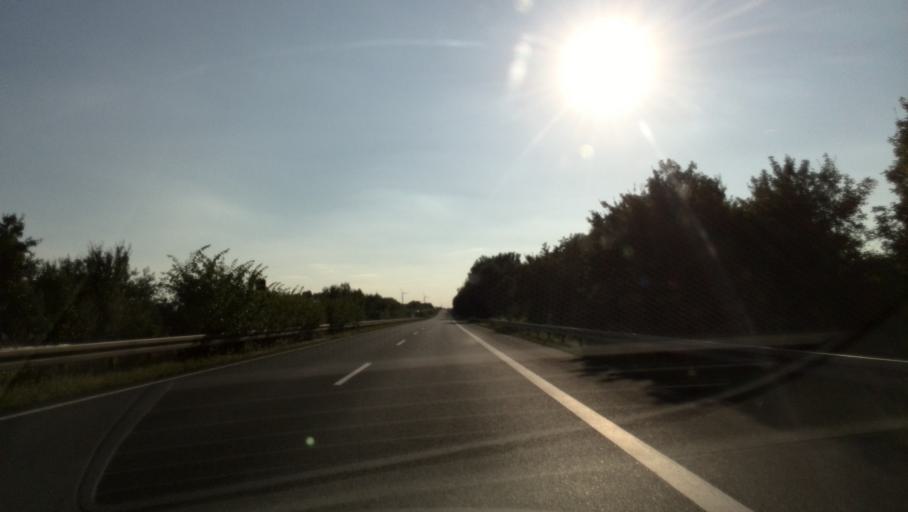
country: DE
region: Lower Saxony
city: Leiferde
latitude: 52.1965
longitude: 10.4366
